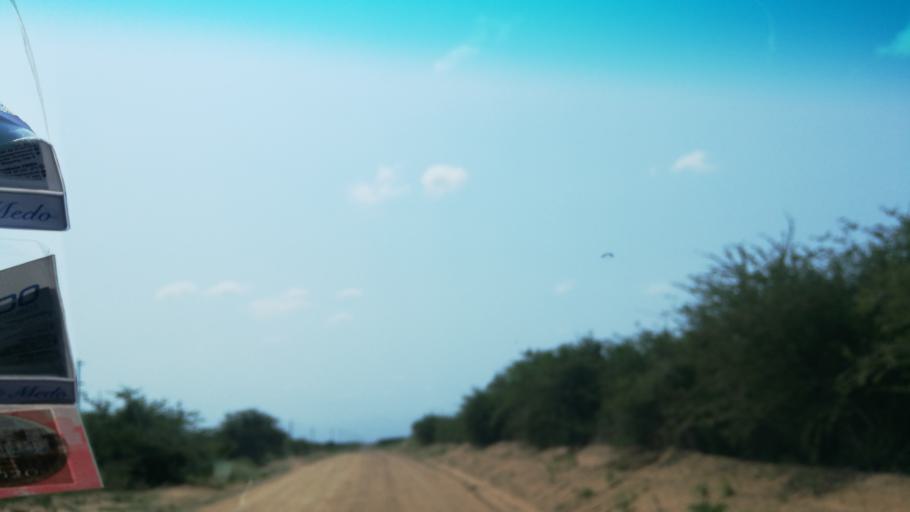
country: MZ
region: Maputo
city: Matola
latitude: -26.0785
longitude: 32.3910
